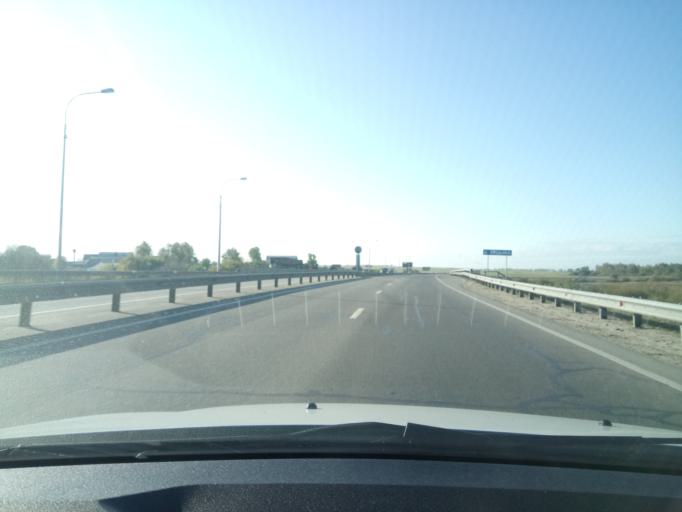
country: RU
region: Nizjnij Novgorod
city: Burevestnik
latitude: 56.1570
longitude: 43.9113
